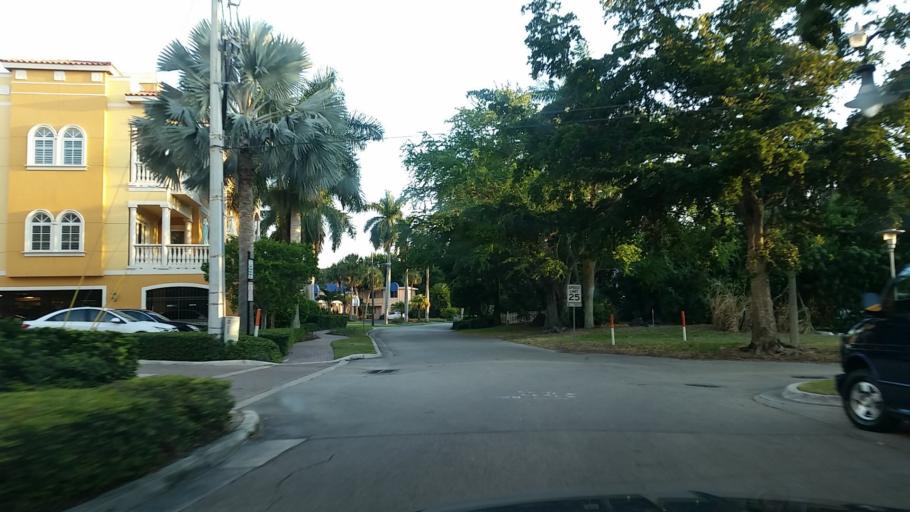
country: US
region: Florida
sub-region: Collier County
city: Naples
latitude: 26.1411
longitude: -81.7995
